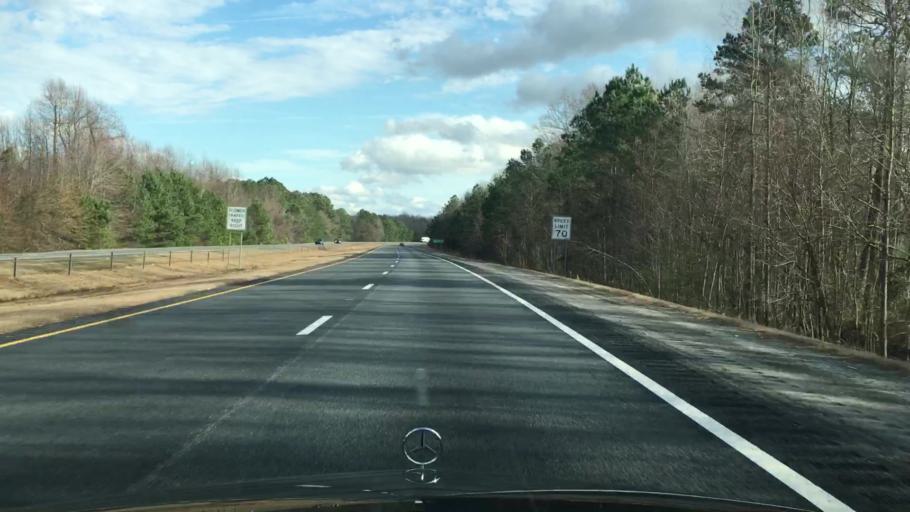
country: US
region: North Carolina
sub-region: Johnston County
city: Four Oaks
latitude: 35.3267
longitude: -78.4376
